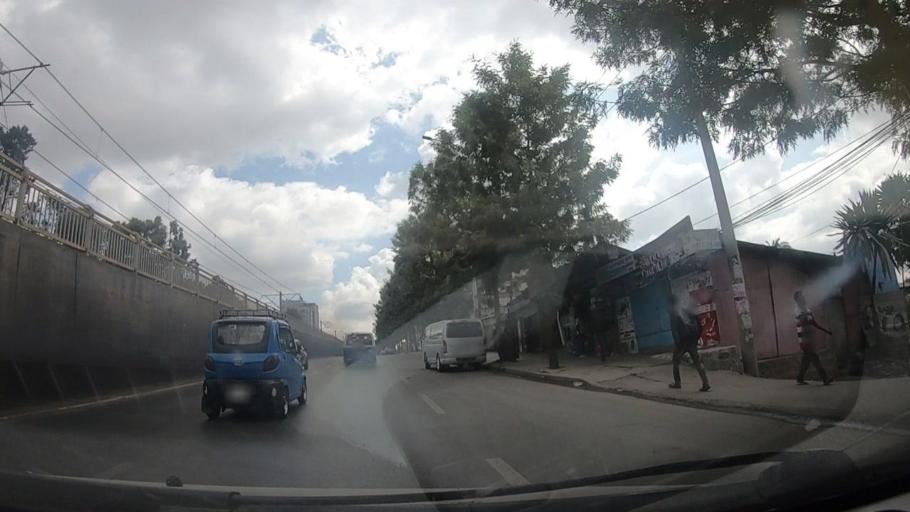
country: ET
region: Adis Abeba
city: Addis Ababa
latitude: 9.0117
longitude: 38.7315
